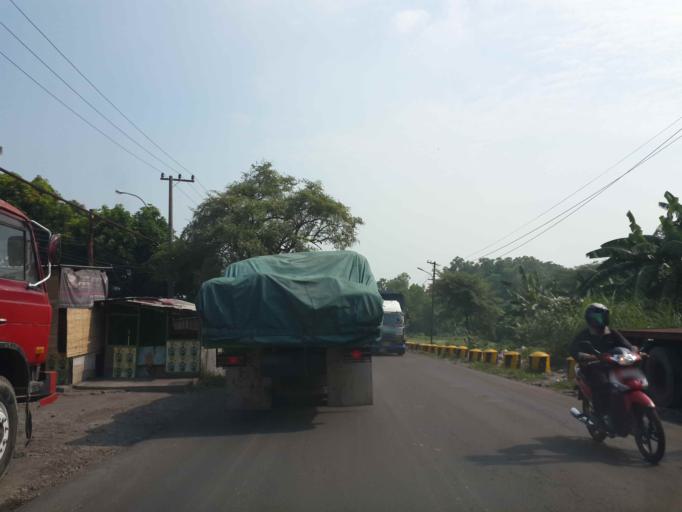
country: ID
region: East Java
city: Gresik
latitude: -7.1721
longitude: 112.6597
